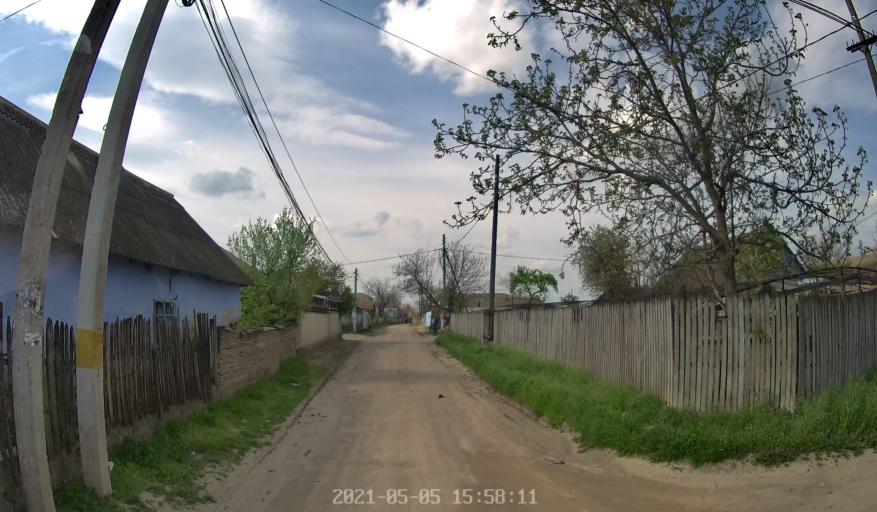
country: MD
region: Criuleni
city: Criuleni
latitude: 47.1376
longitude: 29.2043
